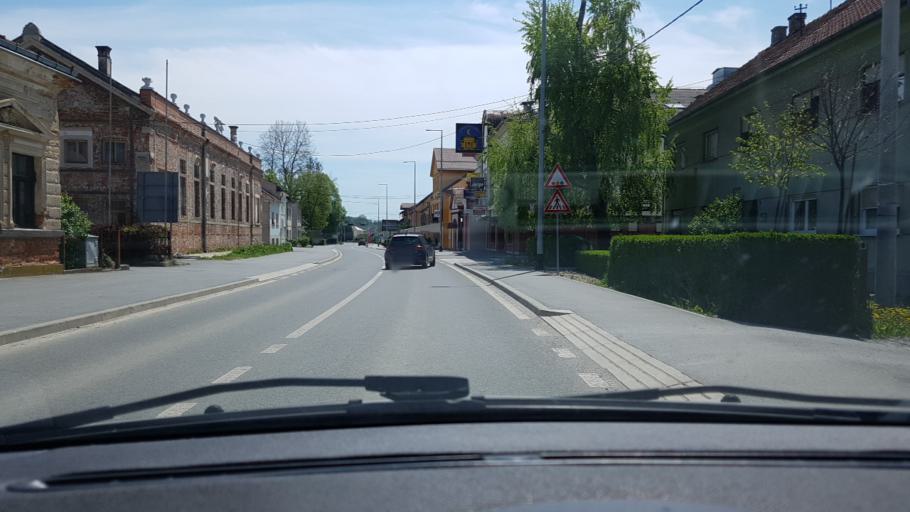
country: HR
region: Krapinsko-Zagorska
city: Zlatar
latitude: 46.0908
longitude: 16.0774
